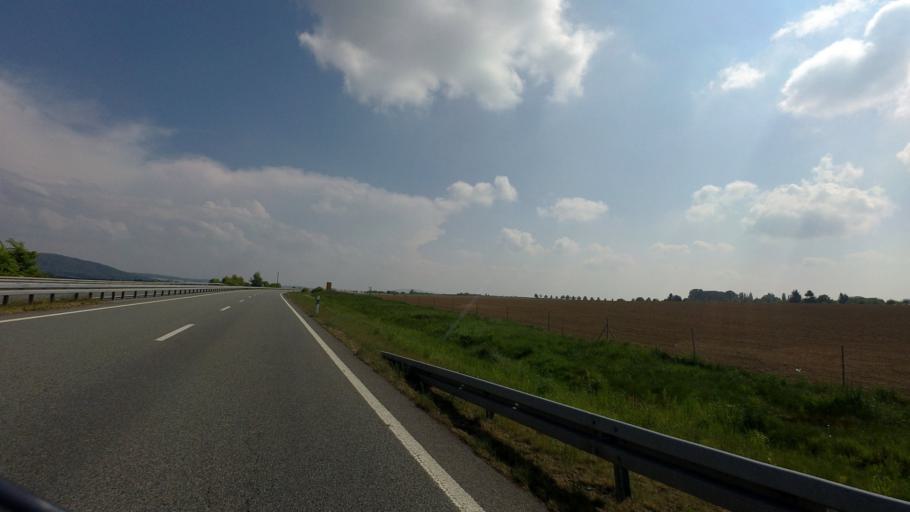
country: DE
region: Saxony
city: Lobau
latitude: 51.1203
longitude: 14.6492
